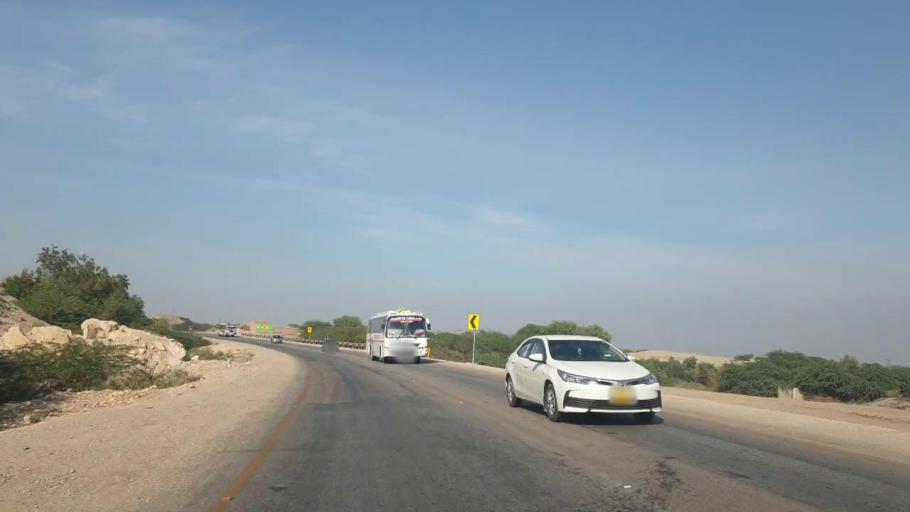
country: PK
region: Sindh
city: Sehwan
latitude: 26.2988
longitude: 67.8949
